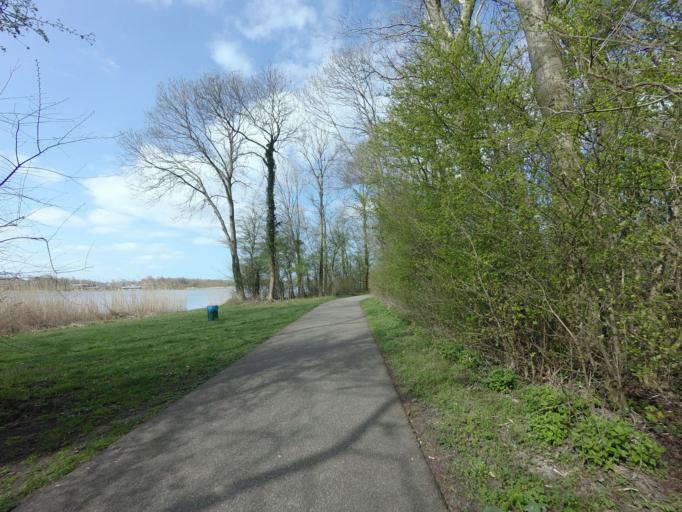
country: NL
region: Utrecht
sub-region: Stichtse Vecht
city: Maarssen
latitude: 52.1431
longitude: 5.0885
